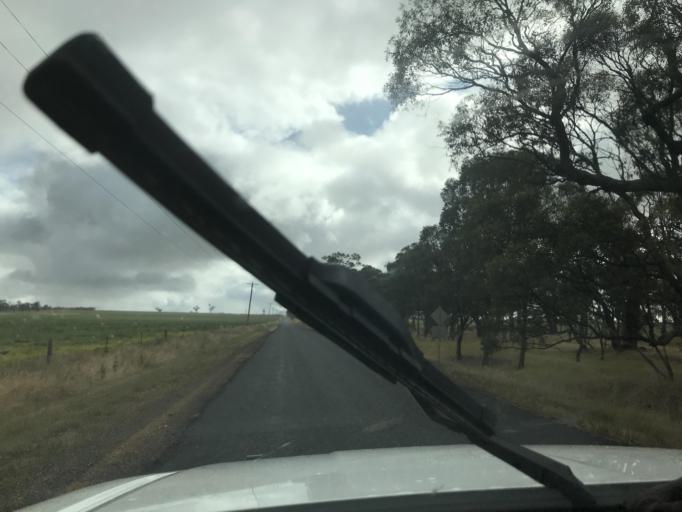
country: AU
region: South Australia
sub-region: Tatiara
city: Bordertown
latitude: -36.3607
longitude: 141.2662
